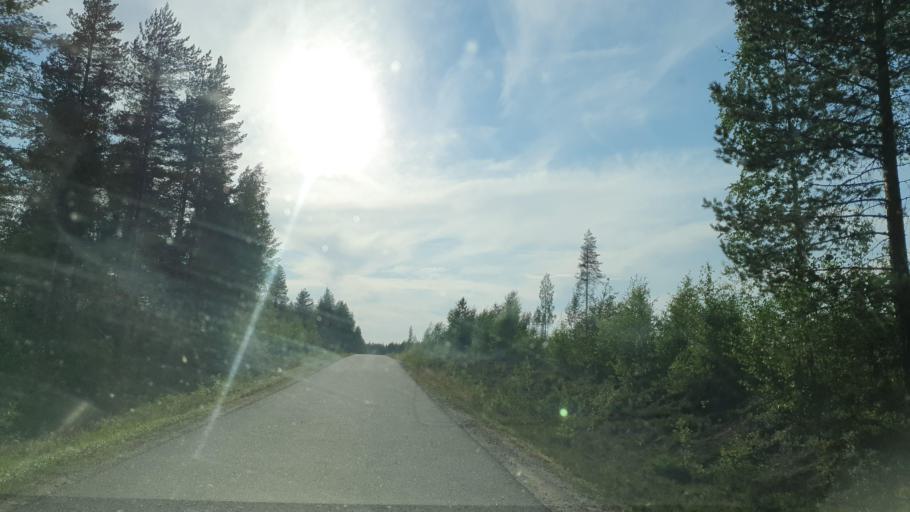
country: FI
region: Kainuu
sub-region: Kehys-Kainuu
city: Kuhmo
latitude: 64.2811
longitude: 29.4096
